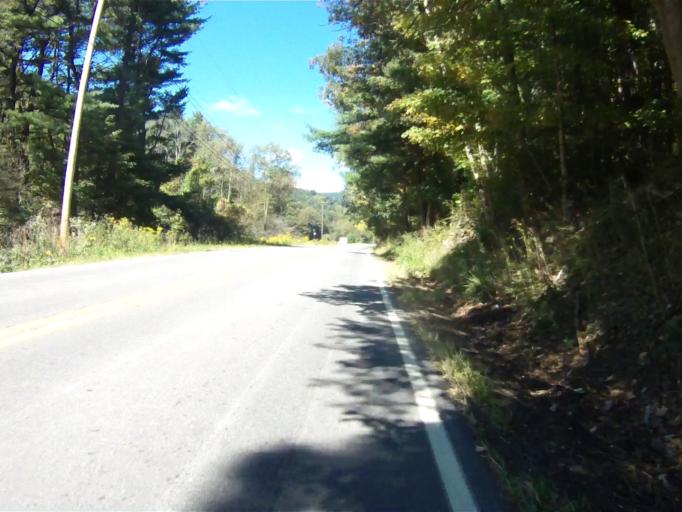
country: US
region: Pennsylvania
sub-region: Centre County
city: Milesburg
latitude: 40.9199
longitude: -77.8948
